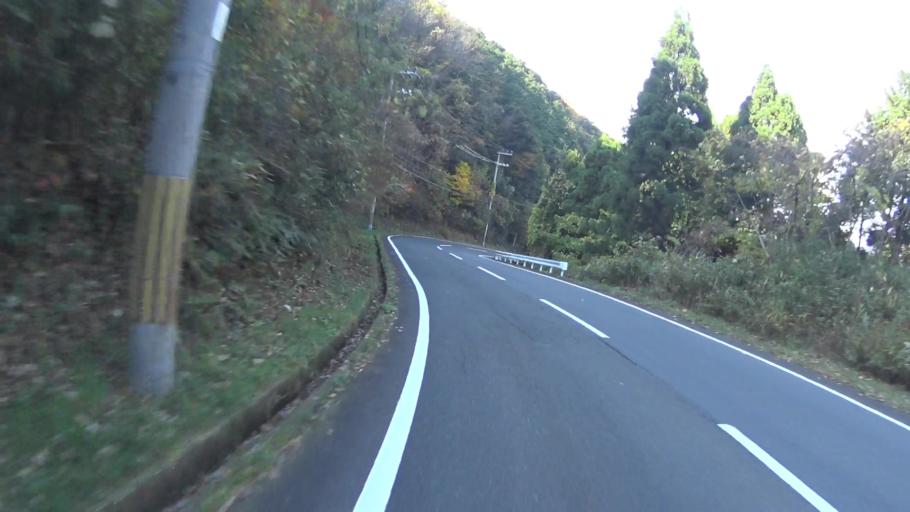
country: JP
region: Kyoto
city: Maizuru
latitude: 35.5421
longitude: 135.3970
